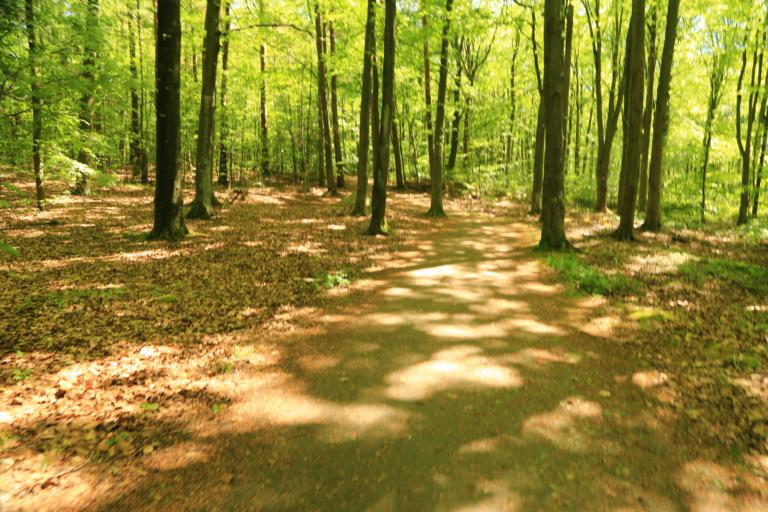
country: SE
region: Halland
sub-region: Varbergs Kommun
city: Varberg
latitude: 57.0976
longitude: 12.2680
